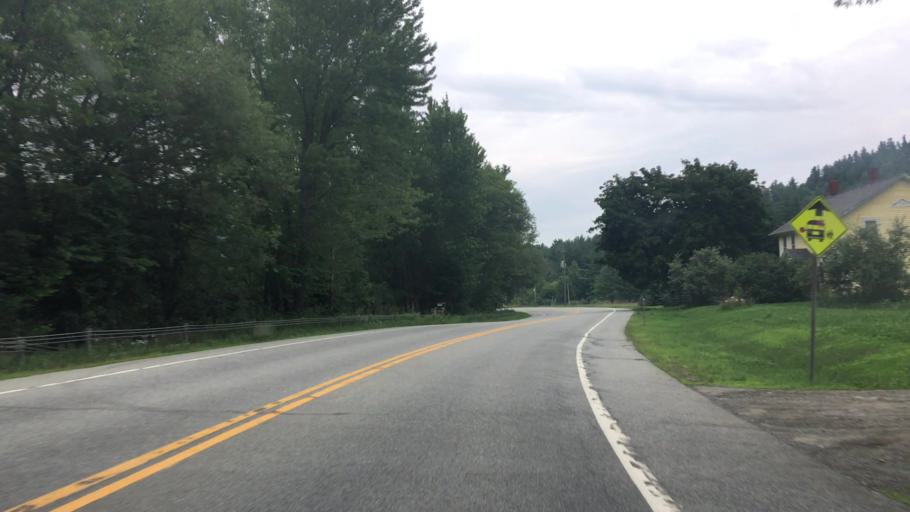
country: US
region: New York
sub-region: Essex County
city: Lake Placid
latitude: 44.3269
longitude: -73.7744
